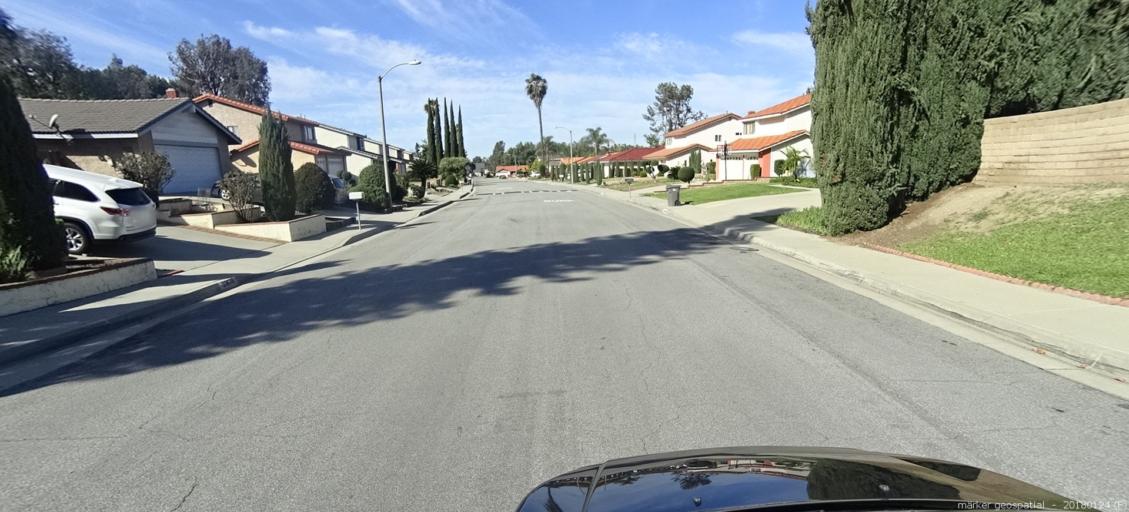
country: US
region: California
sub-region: Los Angeles County
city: Diamond Bar
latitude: 33.9997
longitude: -117.8060
